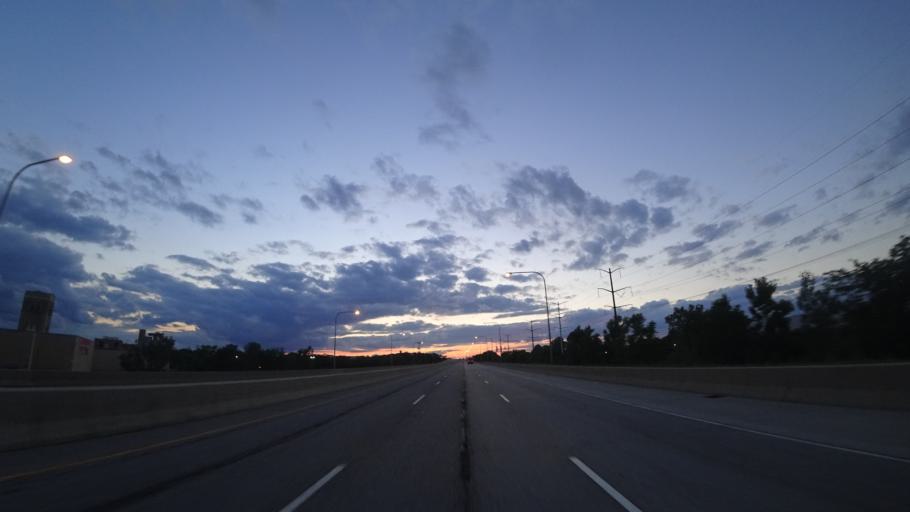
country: US
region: Illinois
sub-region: Cook County
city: Dolton
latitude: 41.7519
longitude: -87.5886
